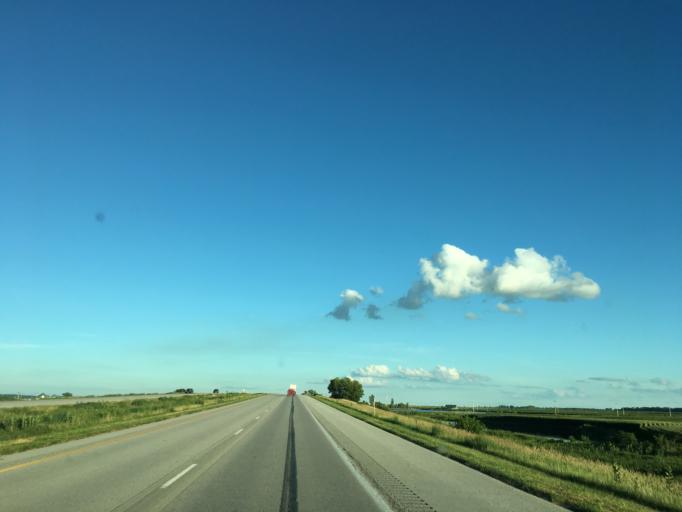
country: US
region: Nebraska
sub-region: Otoe County
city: Nebraska City
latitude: 40.6724
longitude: -95.7688
